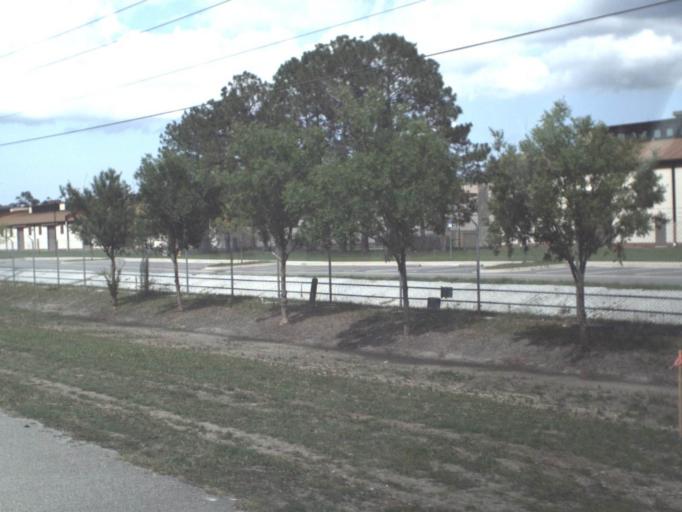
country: US
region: Florida
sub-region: Clay County
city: Orange Park
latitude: 30.2123
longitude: -81.7043
